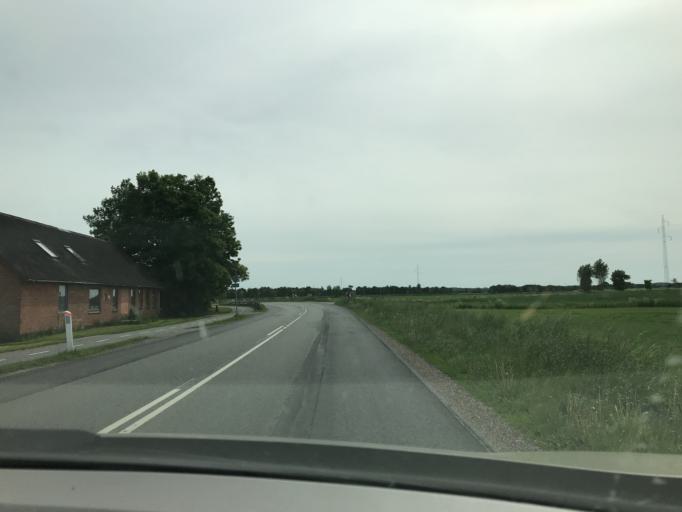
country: DK
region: Central Jutland
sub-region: Norddjurs Kommune
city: Allingabro
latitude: 56.4843
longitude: 10.3208
